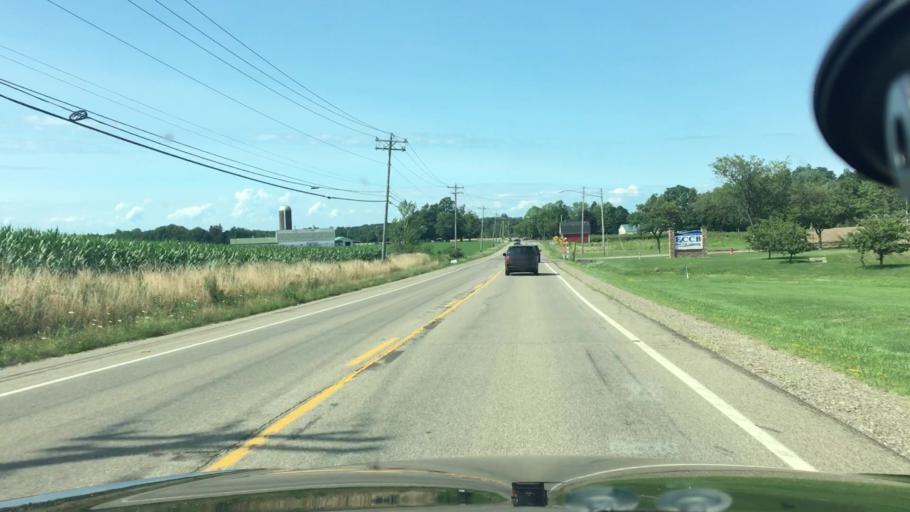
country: US
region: New York
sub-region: Chautauqua County
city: Fredonia
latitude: 42.4164
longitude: -79.3124
